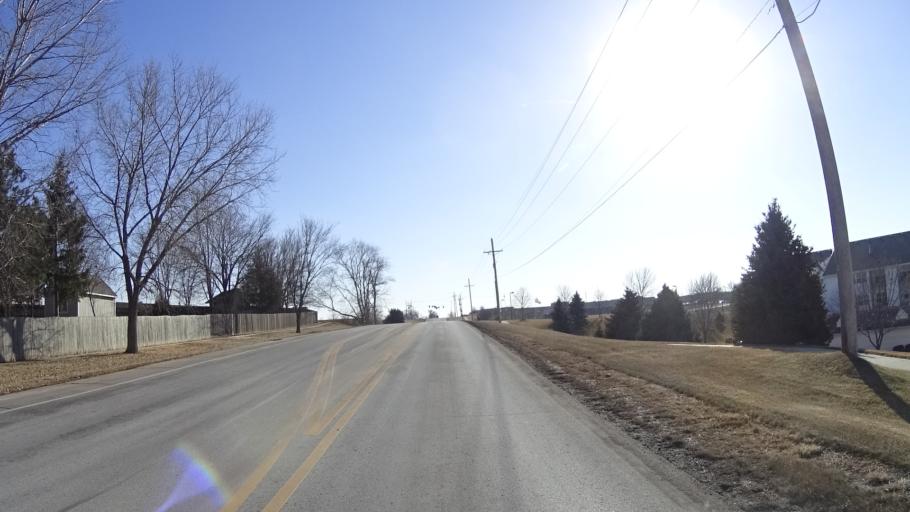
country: US
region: Nebraska
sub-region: Douglas County
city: Bennington
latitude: 41.3093
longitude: -96.1197
